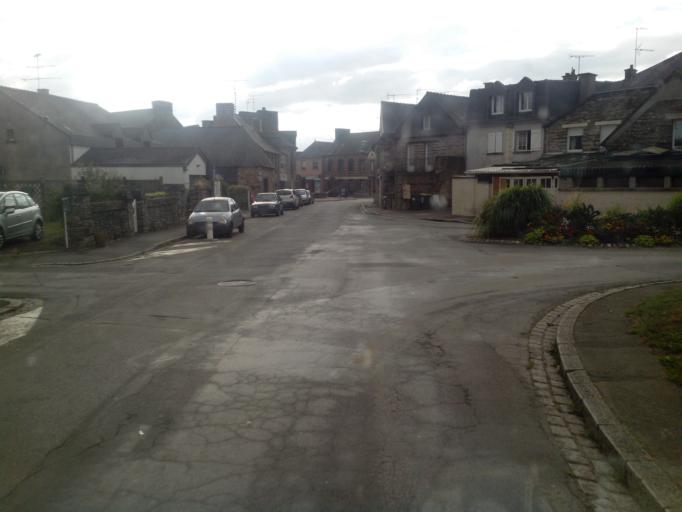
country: FR
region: Brittany
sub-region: Departement d'Ille-et-Vilaine
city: Plelan-le-Grand
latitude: 48.0017
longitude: -2.0973
